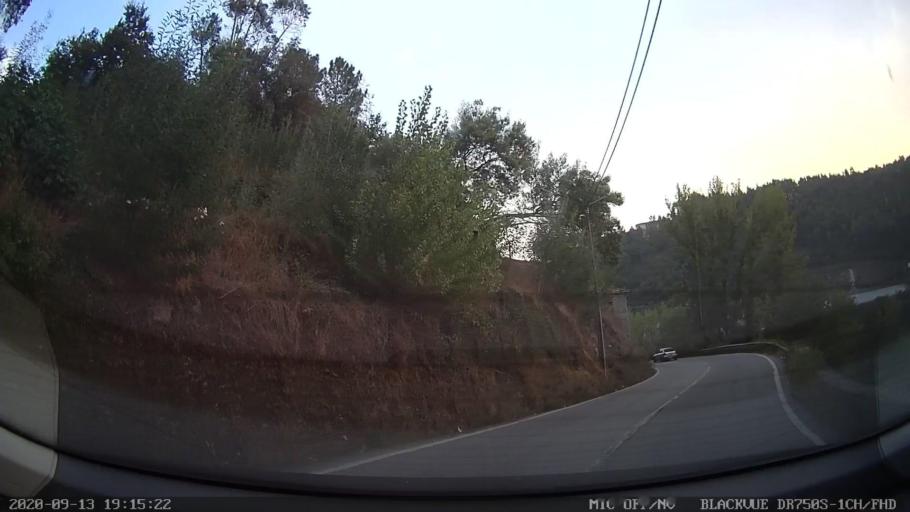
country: PT
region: Porto
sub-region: Amarante
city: Amarante
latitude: 41.2608
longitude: -8.0596
